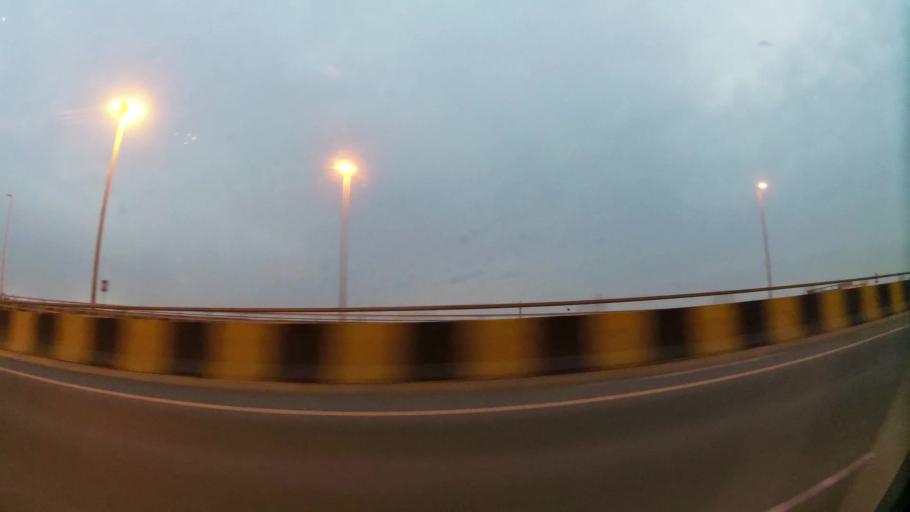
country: BH
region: Northern
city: Madinat `Isa
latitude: 26.1690
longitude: 50.5436
